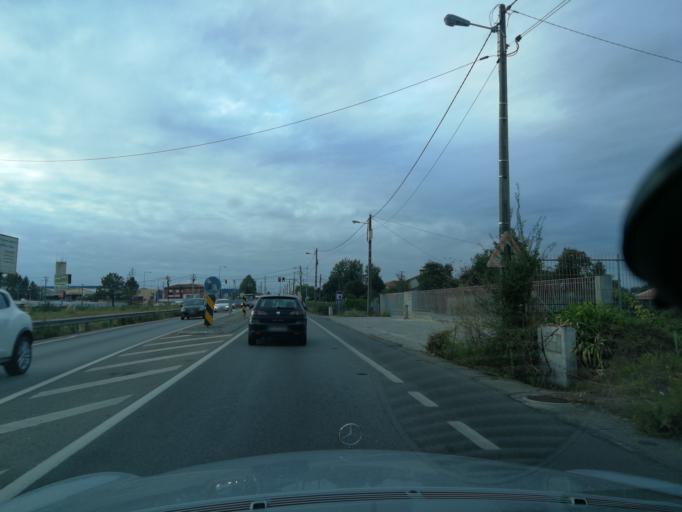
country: PT
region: Aveiro
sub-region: Agueda
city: Agueda
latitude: 40.5899
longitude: -8.4518
